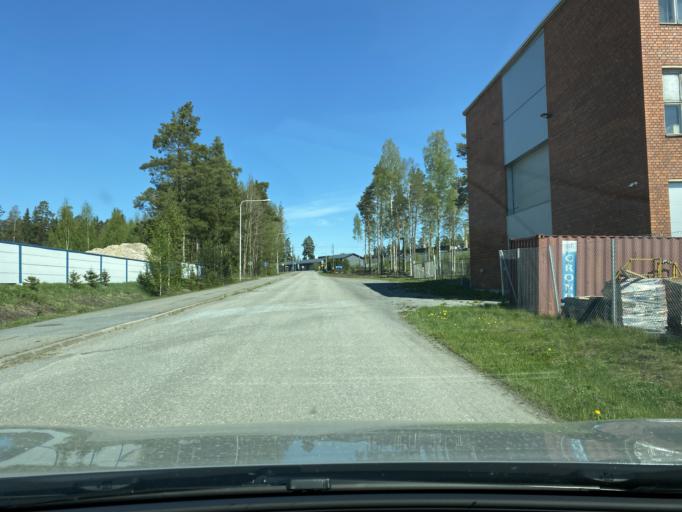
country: FI
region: Pirkanmaa
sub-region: Lounais-Pirkanmaa
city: Vammala
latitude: 61.3527
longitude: 22.8811
